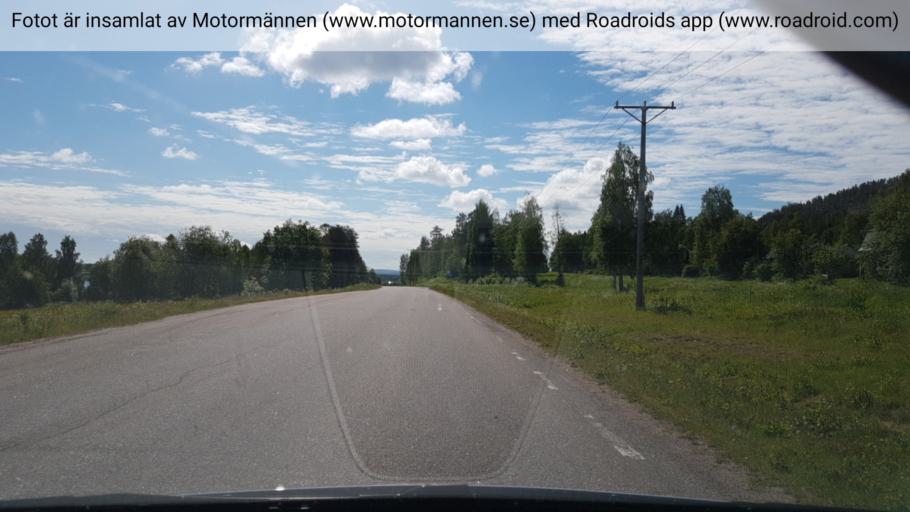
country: FI
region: Lapland
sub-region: Torniolaakso
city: Pello
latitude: 66.6565
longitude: 23.8545
